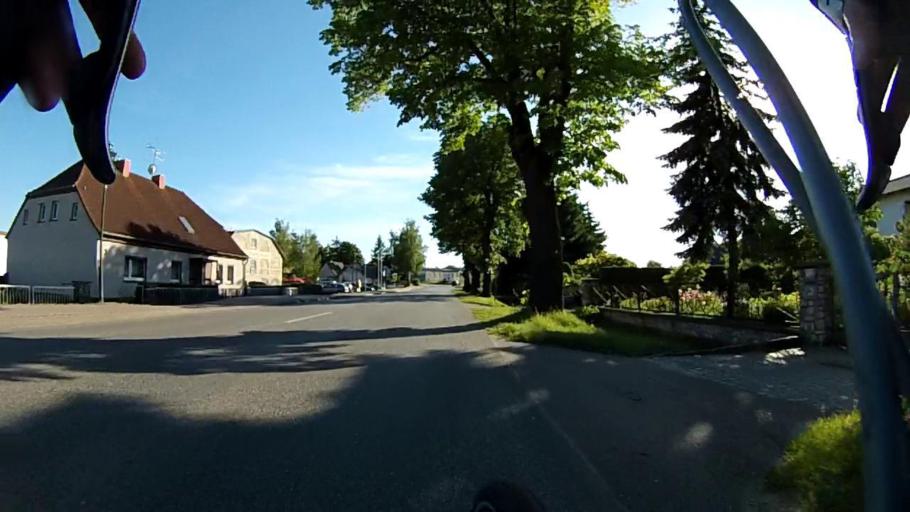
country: DE
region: Brandenburg
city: Ahrensfelde
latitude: 52.6067
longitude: 13.6197
